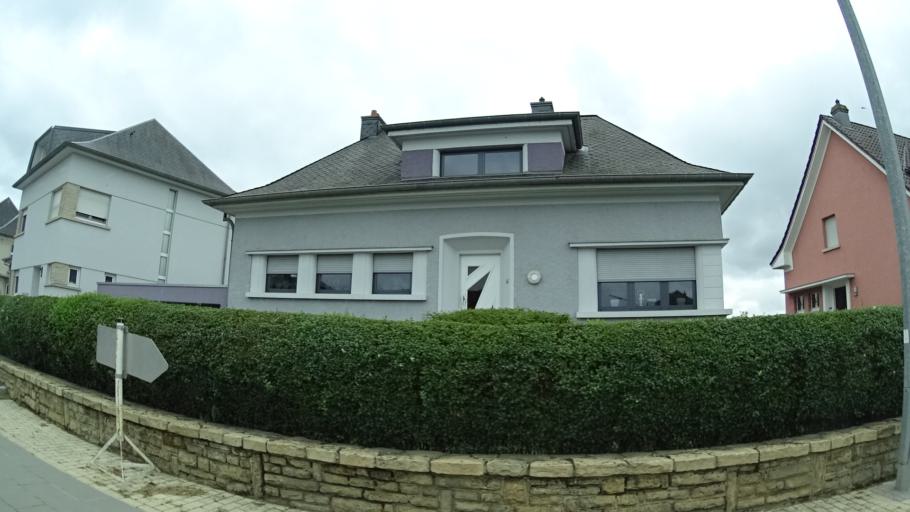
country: LU
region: Luxembourg
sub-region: Canton d'Esch-sur-Alzette
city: Bettembourg
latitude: 49.5183
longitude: 6.0935
